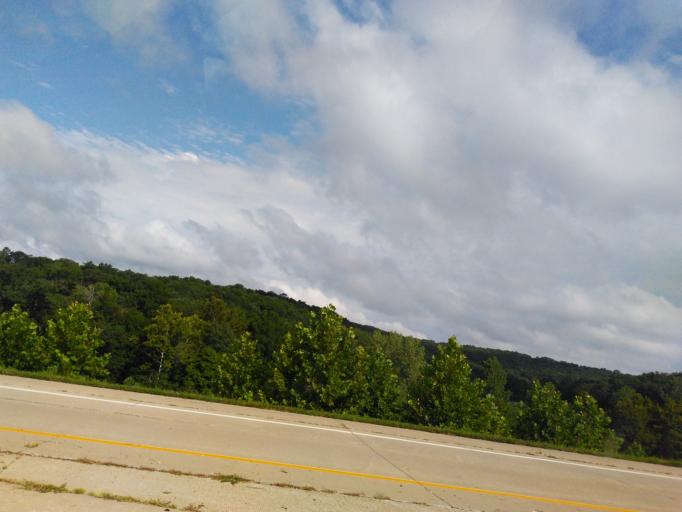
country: US
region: Missouri
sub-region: Jefferson County
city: Hillsboro
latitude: 38.3109
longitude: -90.5363
